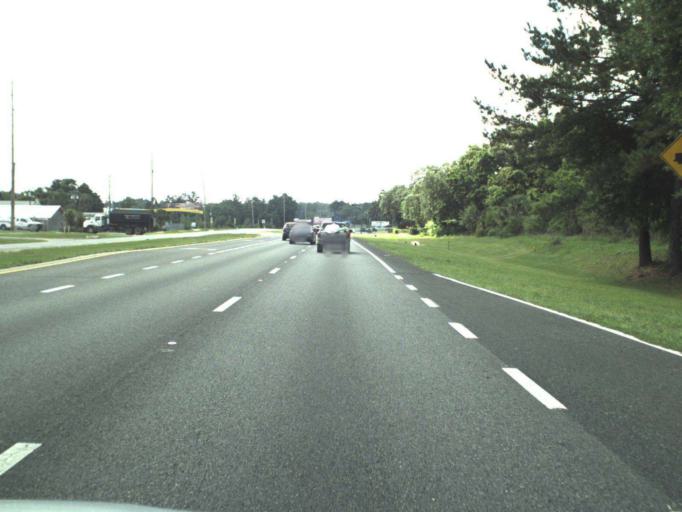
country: US
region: Florida
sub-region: Marion County
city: Ocala
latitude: 29.1596
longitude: -82.0895
